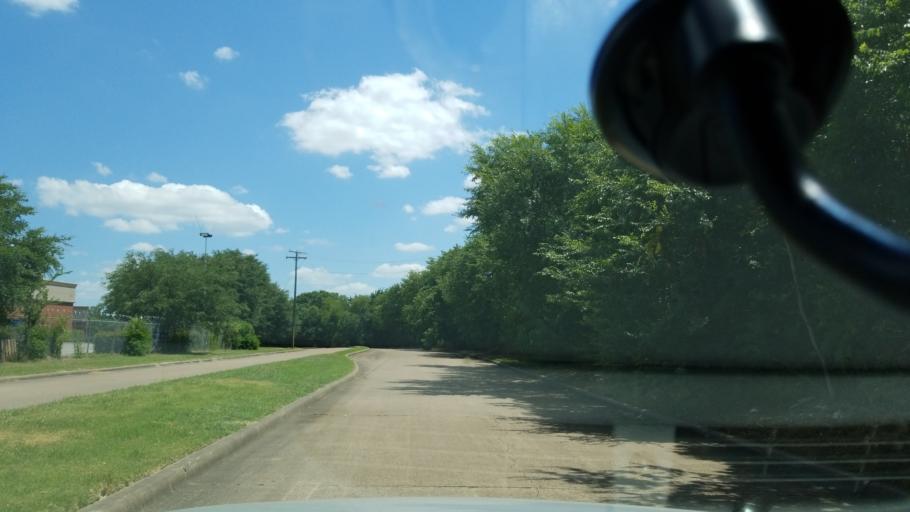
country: US
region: Texas
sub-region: Dallas County
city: Cockrell Hill
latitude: 32.6928
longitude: -96.8305
